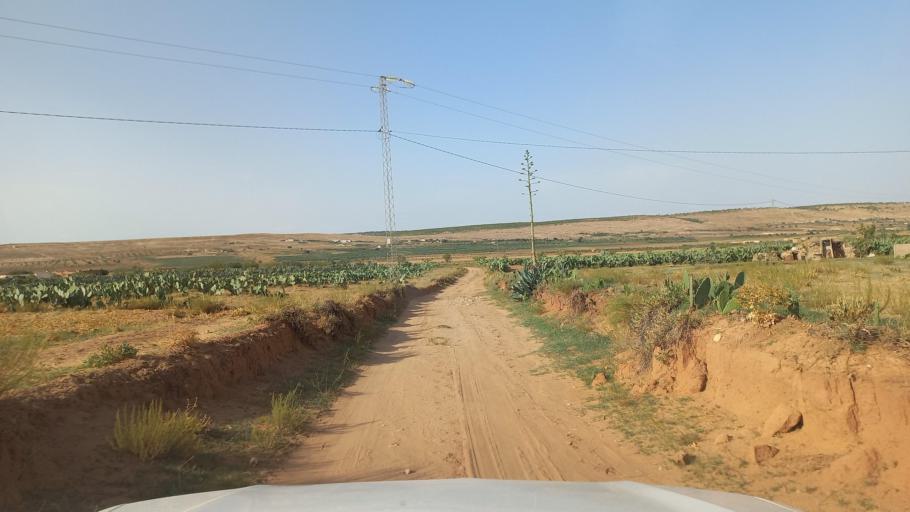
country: TN
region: Al Qasrayn
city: Kasserine
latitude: 35.3488
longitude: 8.8486
